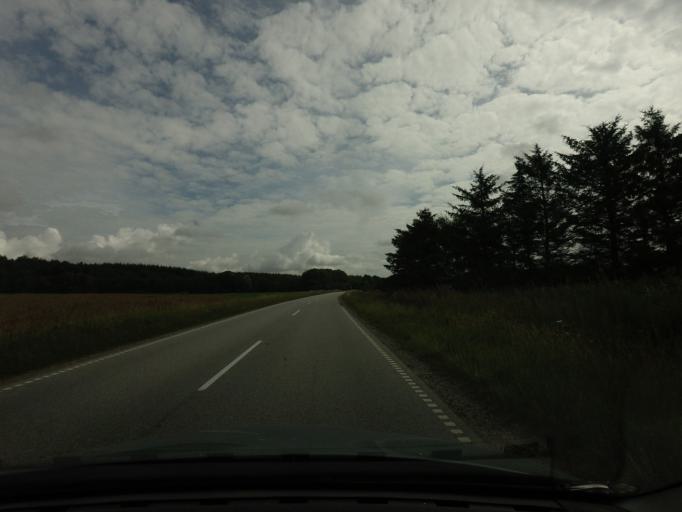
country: DK
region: North Denmark
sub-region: Bronderslev Kommune
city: Hjallerup
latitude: 57.2817
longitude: 10.1957
